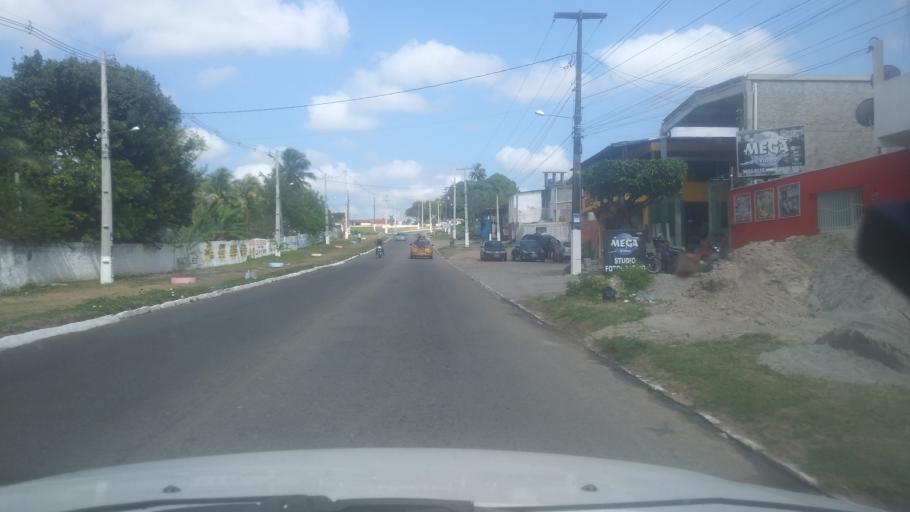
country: BR
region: Rio Grande do Norte
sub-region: Extremoz
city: Extremoz
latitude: -5.7041
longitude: -35.2838
